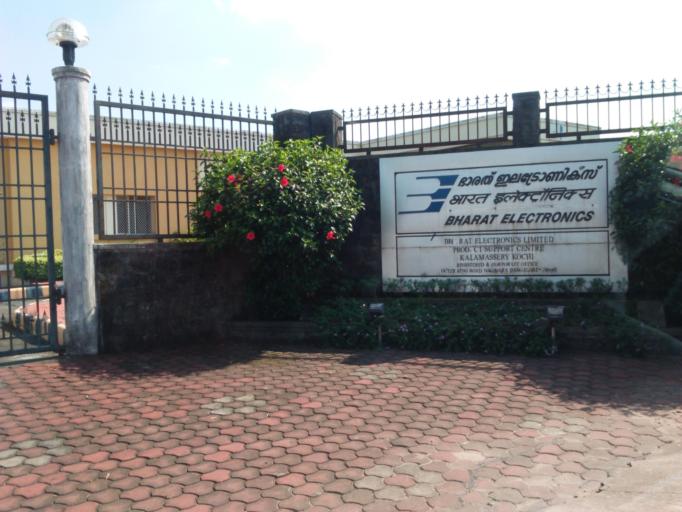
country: IN
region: Kerala
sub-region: Ernakulam
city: Aluva
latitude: 10.0577
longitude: 76.3605
